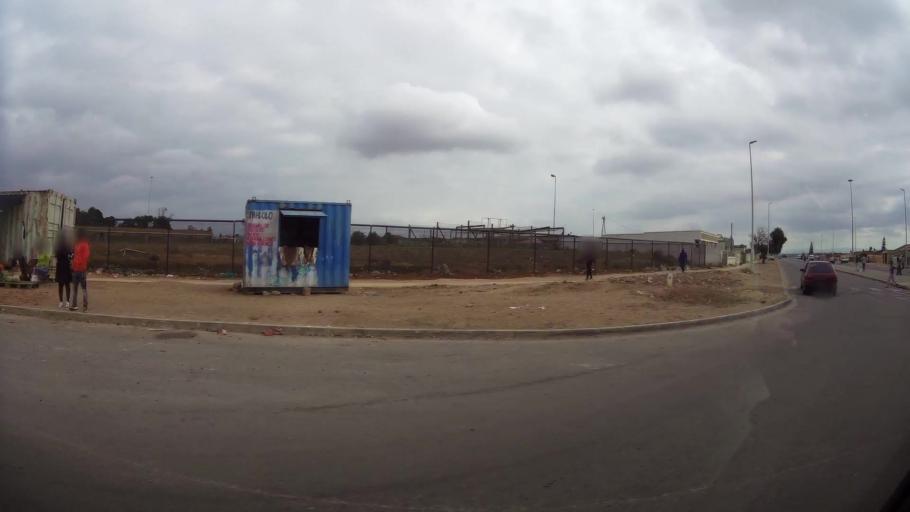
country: ZA
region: Eastern Cape
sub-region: Nelson Mandela Bay Metropolitan Municipality
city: Port Elizabeth
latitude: -33.8693
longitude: 25.5652
